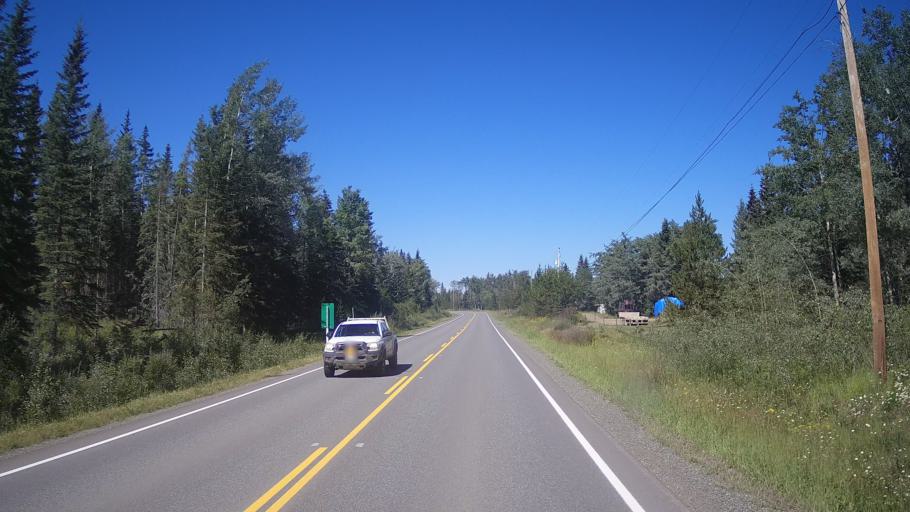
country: CA
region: British Columbia
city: Cache Creek
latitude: 51.5472
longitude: -120.9221
